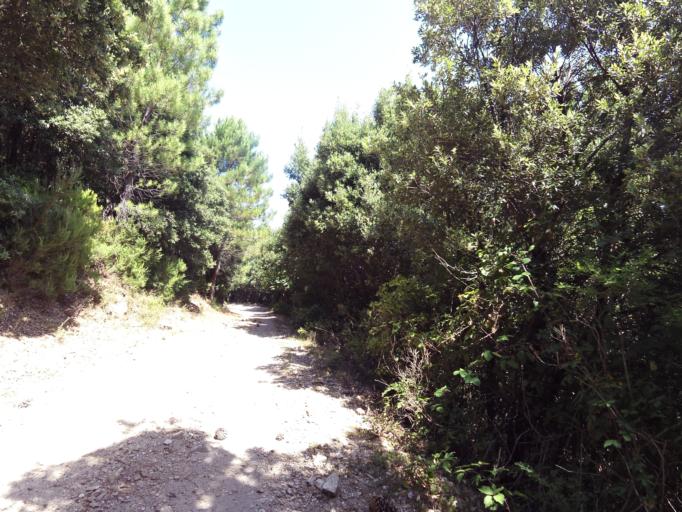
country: IT
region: Calabria
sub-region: Provincia di Reggio Calabria
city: Bivongi
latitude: 38.5110
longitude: 16.4318
